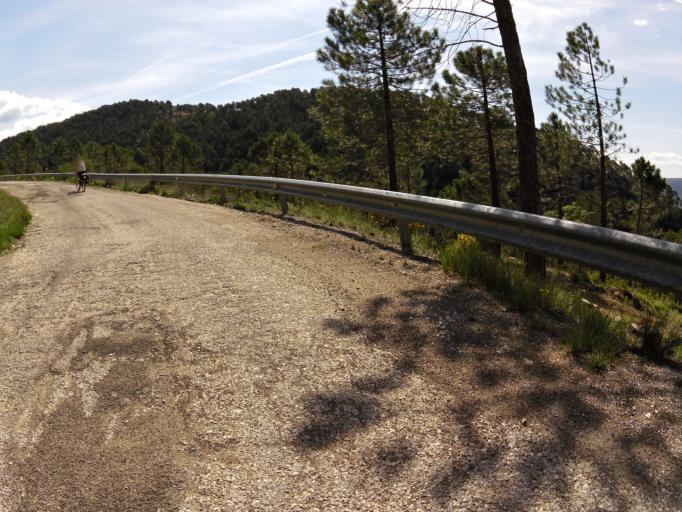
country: ES
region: Castille-La Mancha
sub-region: Provincia de Albacete
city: Riopar
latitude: 38.5238
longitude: -2.4323
